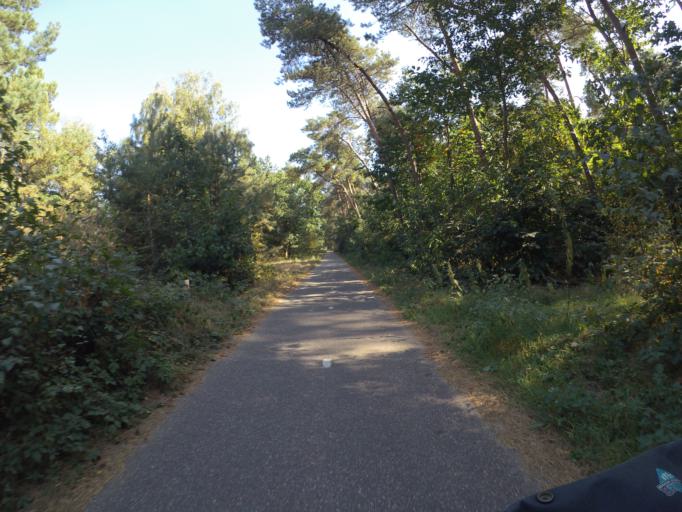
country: NL
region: North Brabant
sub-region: Gemeente Oirschot
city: Oirschot
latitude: 51.4622
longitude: 5.3168
